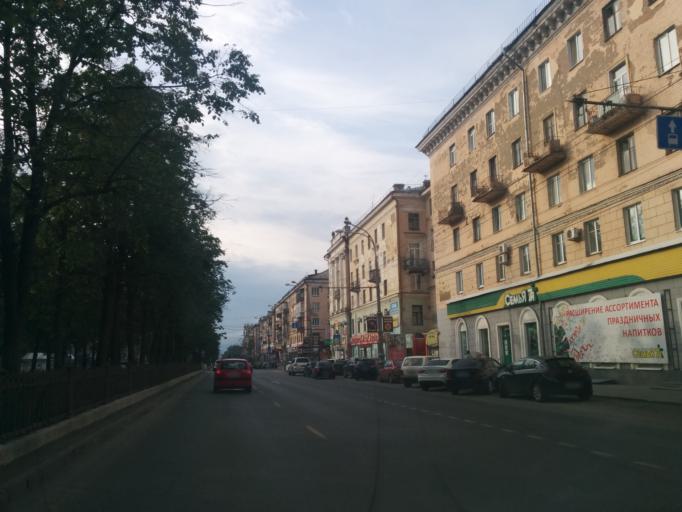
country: RU
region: Perm
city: Perm
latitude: 57.9976
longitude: 56.2521
